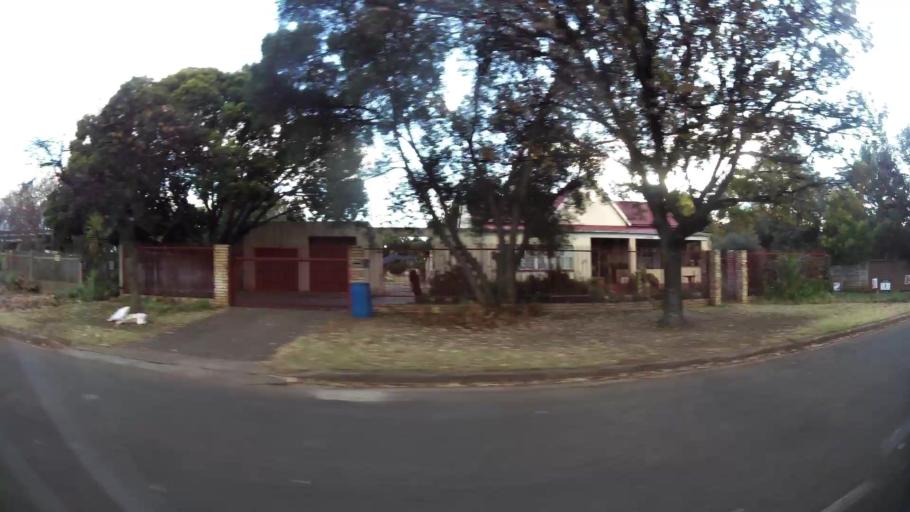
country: ZA
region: North-West
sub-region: Dr Kenneth Kaunda District Municipality
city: Potchefstroom
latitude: -26.7192
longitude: 27.0886
